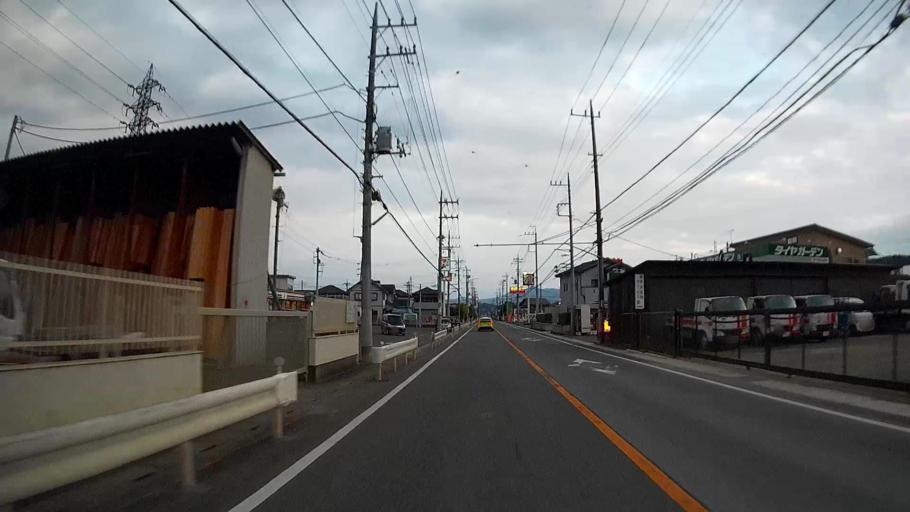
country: JP
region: Saitama
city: Chichibu
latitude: 35.9780
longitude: 139.0727
